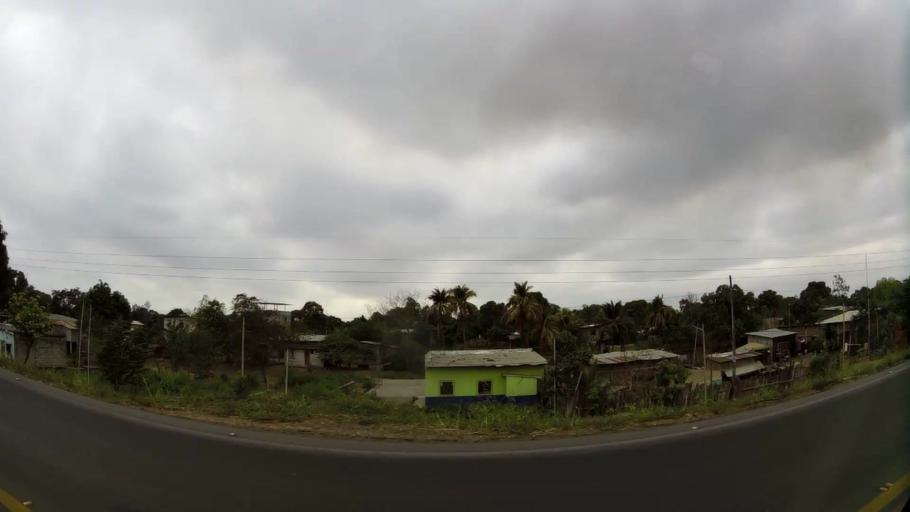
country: EC
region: Guayas
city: Yaguachi Nuevo
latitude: -2.2567
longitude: -79.6363
